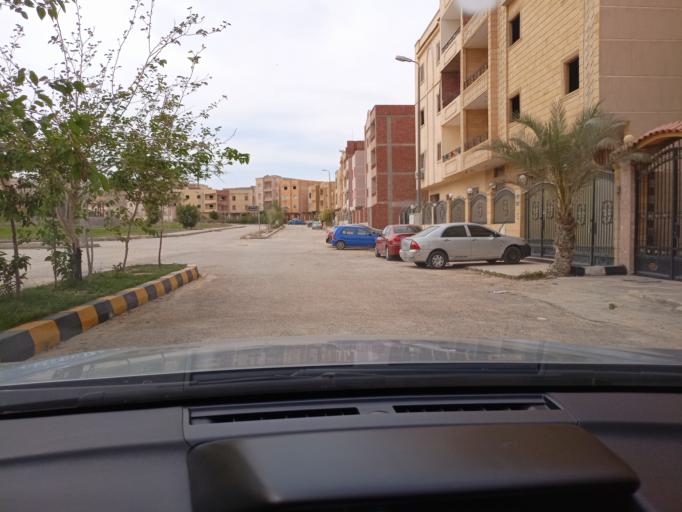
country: EG
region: Muhafazat al Qalyubiyah
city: Al Khankah
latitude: 30.2452
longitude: 31.4974
